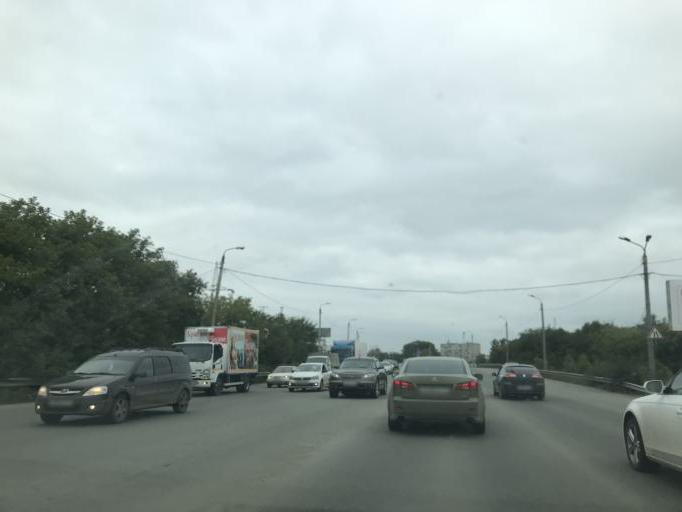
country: RU
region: Chelyabinsk
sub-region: Gorod Chelyabinsk
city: Chelyabinsk
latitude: 55.1659
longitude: 61.4284
